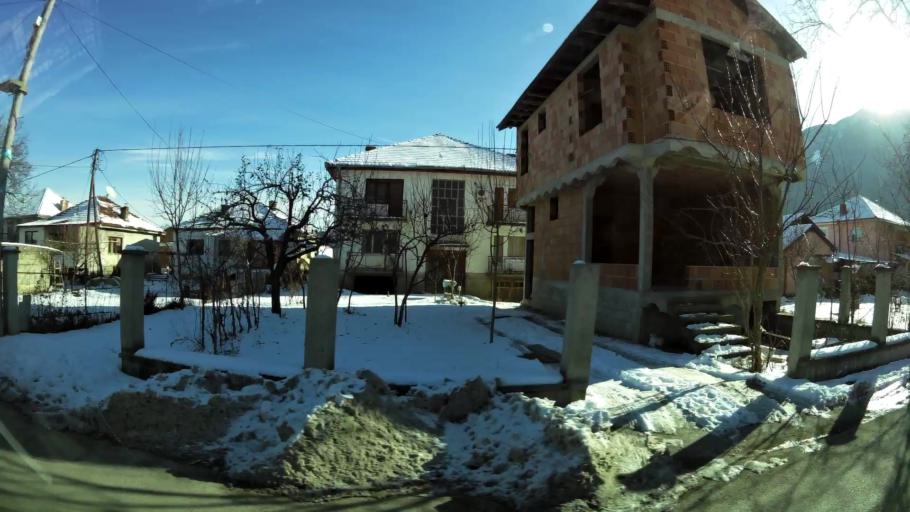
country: MK
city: Grchec
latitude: 41.9772
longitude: 21.3091
